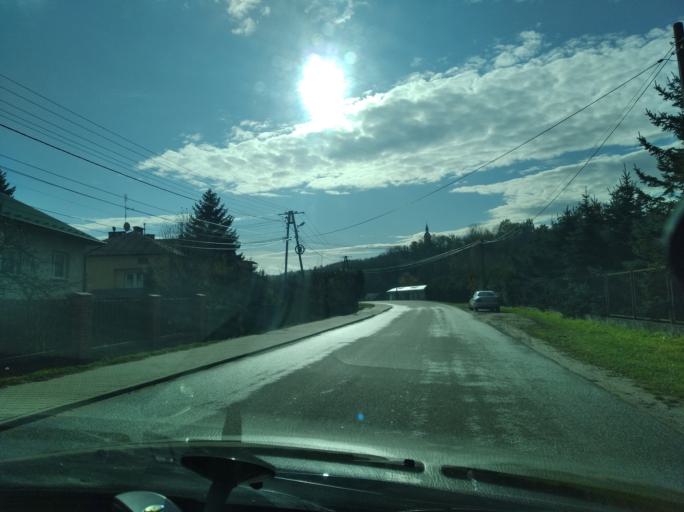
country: PL
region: Subcarpathian Voivodeship
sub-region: Powiat debicki
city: Brzeznica
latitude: 50.0531
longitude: 21.4842
